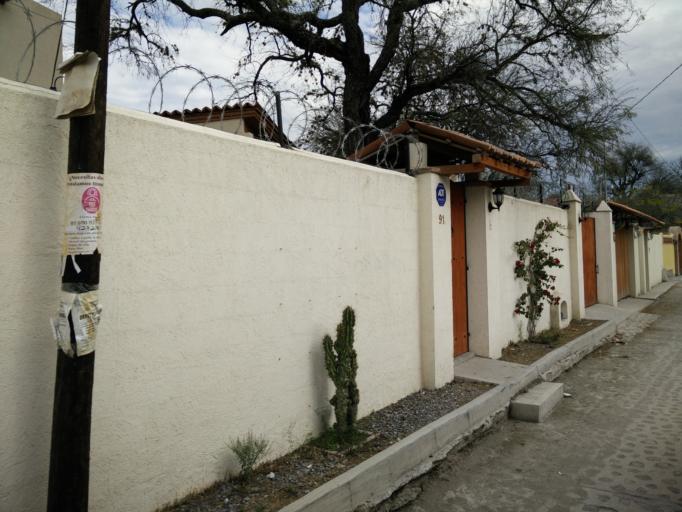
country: MX
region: Queretaro
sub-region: Tequisquiapan
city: Tequisquiapan
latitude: 20.5321
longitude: -99.8953
